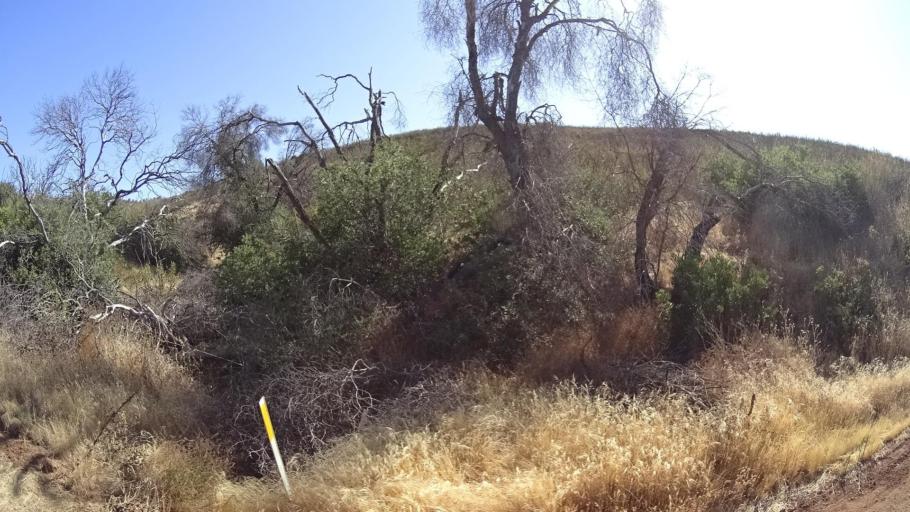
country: US
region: California
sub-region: Mariposa County
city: Mariposa
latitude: 37.6262
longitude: -120.2439
